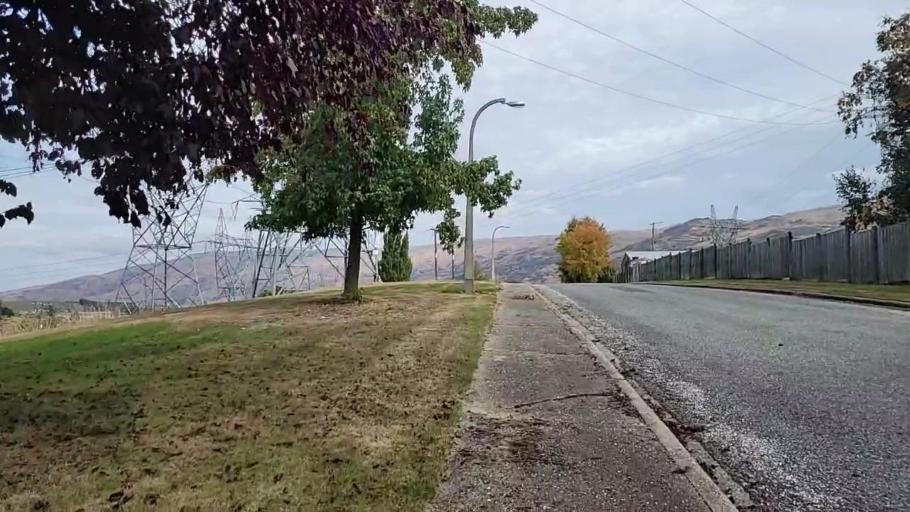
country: NZ
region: Otago
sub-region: Queenstown-Lakes District
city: Kingston
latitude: -45.4766
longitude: 169.3184
